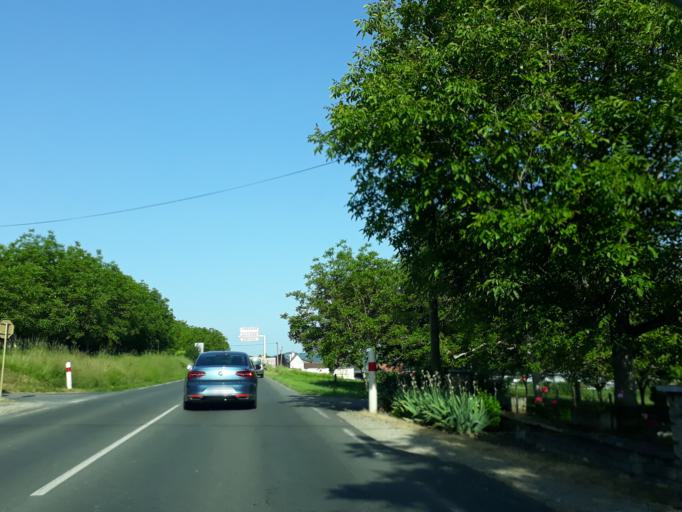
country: FR
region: Aquitaine
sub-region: Departement de la Dordogne
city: Terrasson-Lavilledieu
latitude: 45.1280
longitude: 1.3330
